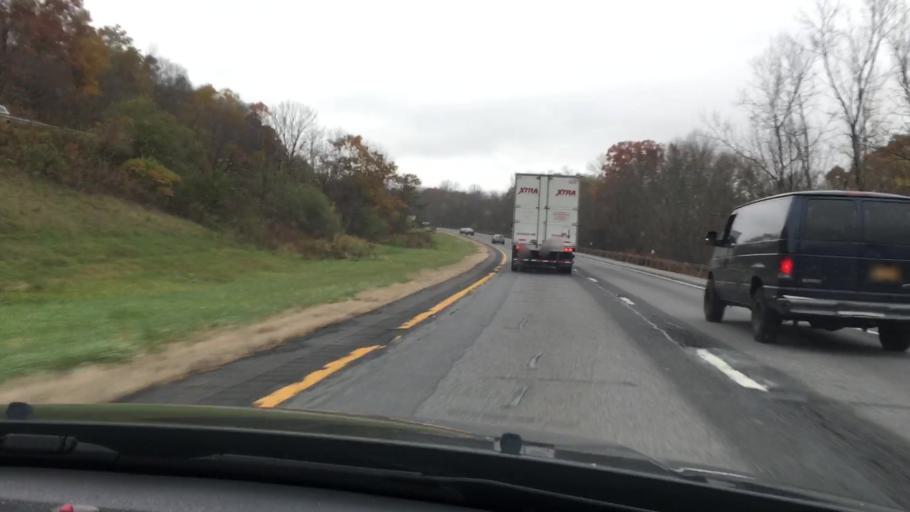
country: US
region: New York
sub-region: Putnam County
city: Lake Carmel
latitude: 41.4980
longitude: -73.6686
